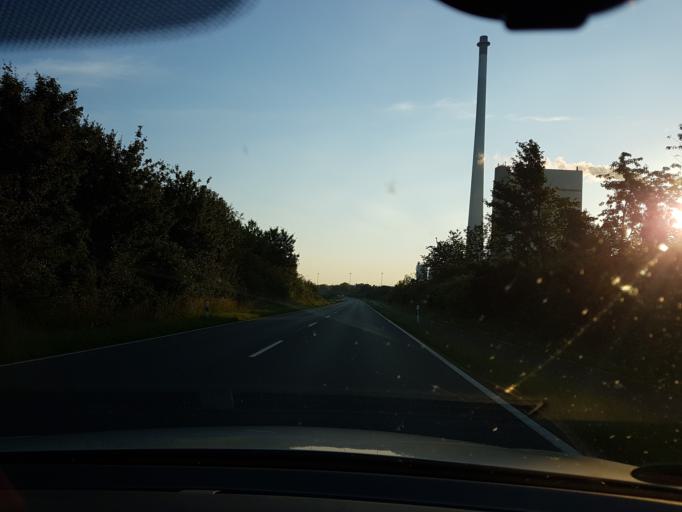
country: DE
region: Lower Saxony
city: Schoningen
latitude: 52.1677
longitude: 10.9712
